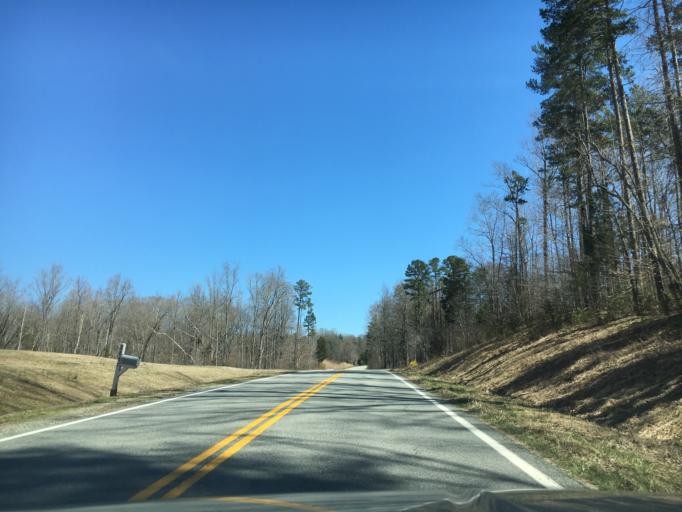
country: US
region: Virginia
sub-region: Halifax County
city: Halifax
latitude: 36.7601
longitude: -78.9052
